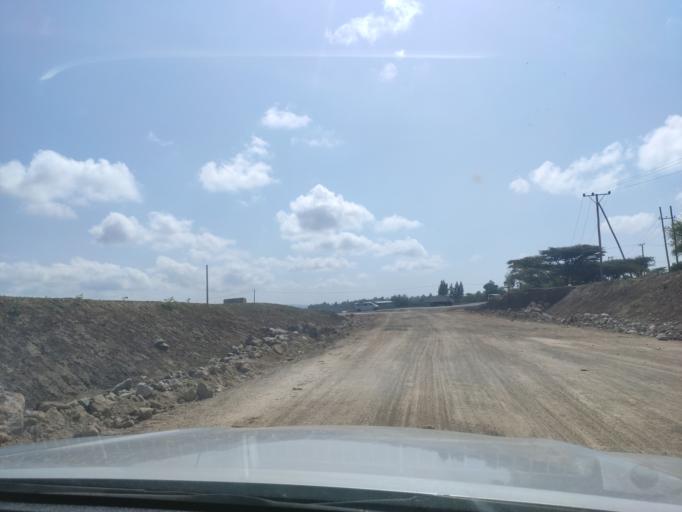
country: ET
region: Oromiya
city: Mojo
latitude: 8.5667
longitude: 39.1643
